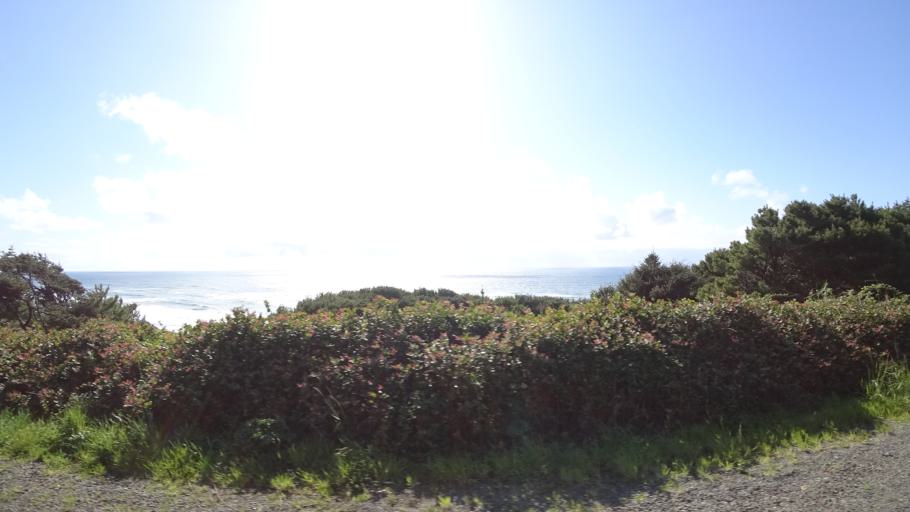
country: US
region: Oregon
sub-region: Lincoln County
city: Waldport
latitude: 44.2123
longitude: -124.1132
